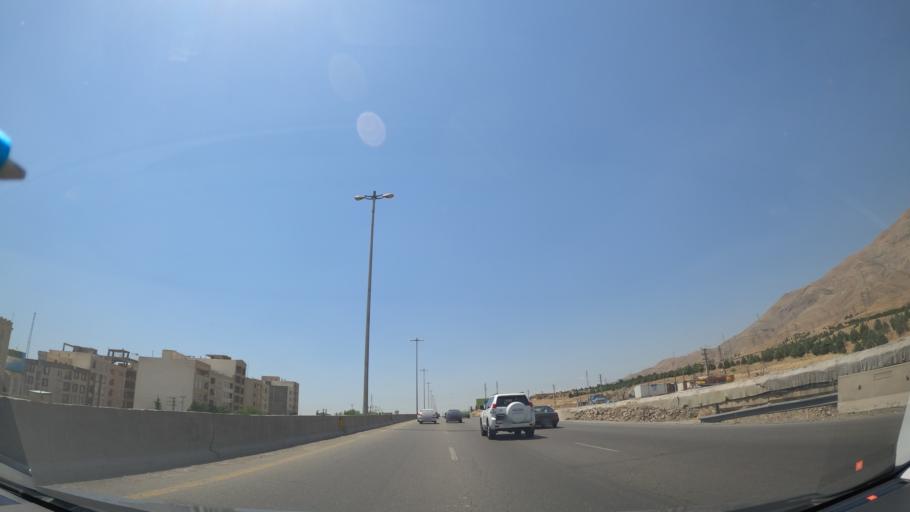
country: IR
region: Tehran
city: Shahr-e Qods
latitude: 35.7582
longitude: 51.0684
